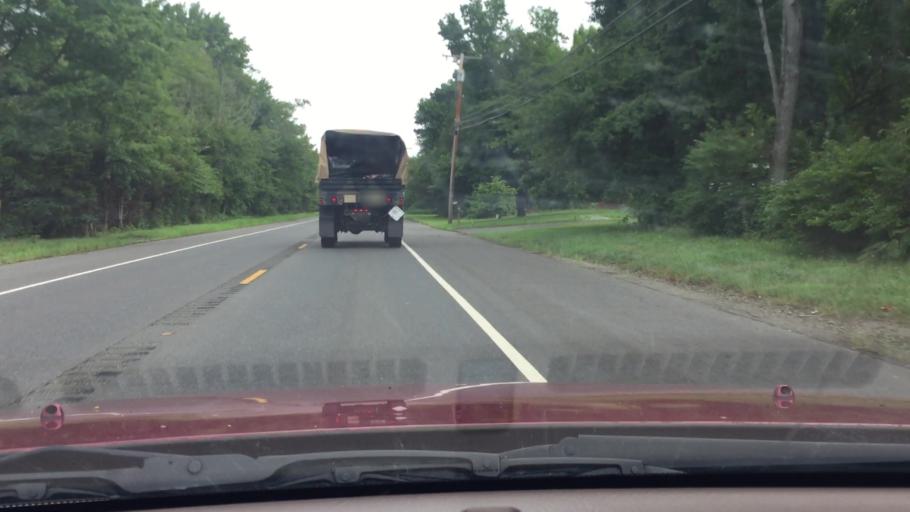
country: US
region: New Jersey
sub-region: Burlington County
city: Fort Dix
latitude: 40.0472
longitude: -74.6468
